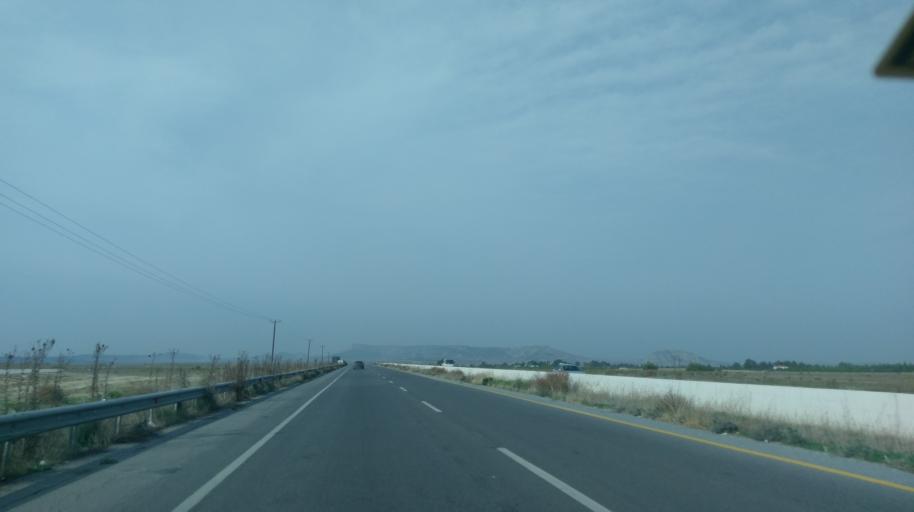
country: CY
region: Lefkosia
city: Mammari
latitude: 35.2128
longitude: 33.1992
